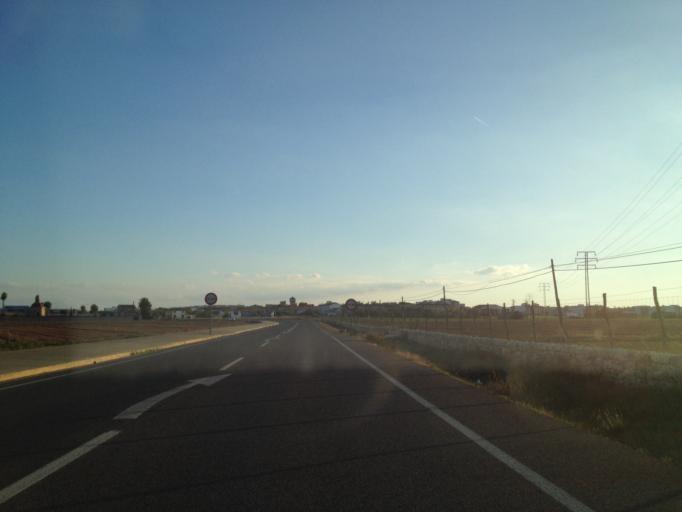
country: ES
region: Balearic Islands
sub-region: Illes Balears
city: sa Pobla
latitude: 39.7810
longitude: 3.0226
